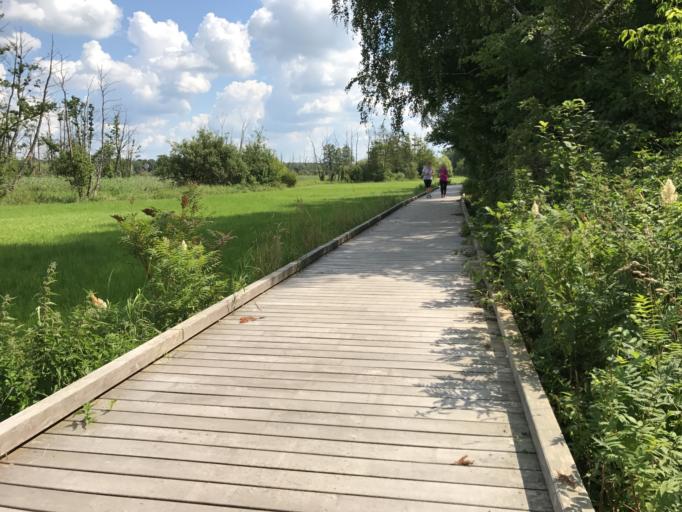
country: DE
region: Berlin
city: Lubars
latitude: 52.6227
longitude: 13.3398
